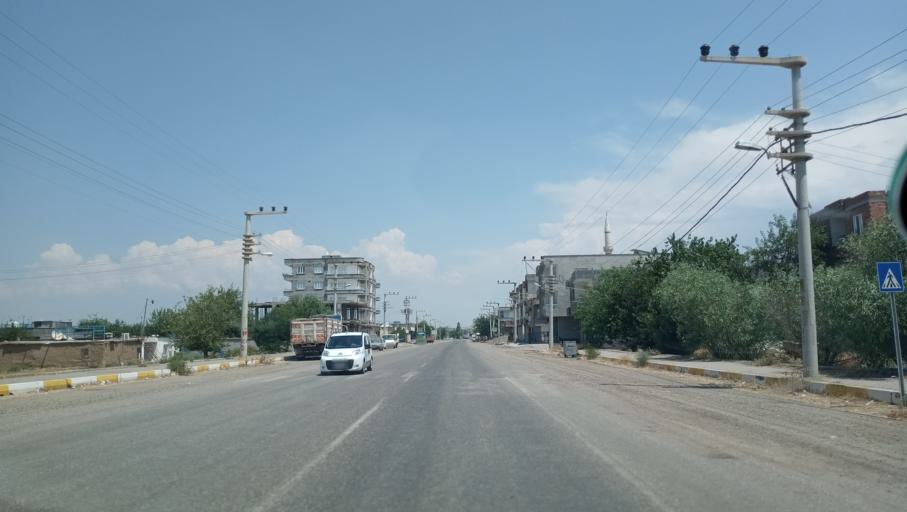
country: TR
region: Diyarbakir
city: Tepe
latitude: 37.7928
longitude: 40.7642
